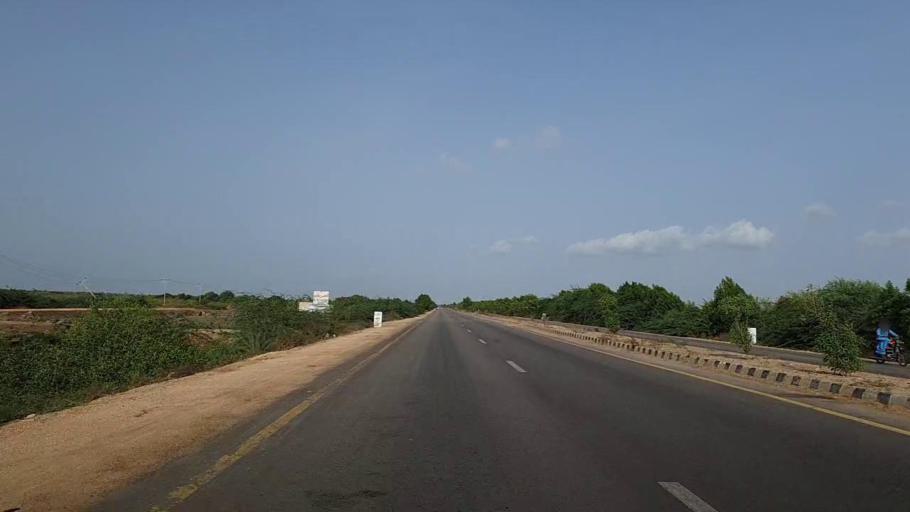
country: PK
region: Sindh
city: Thatta
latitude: 24.7427
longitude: 67.8252
